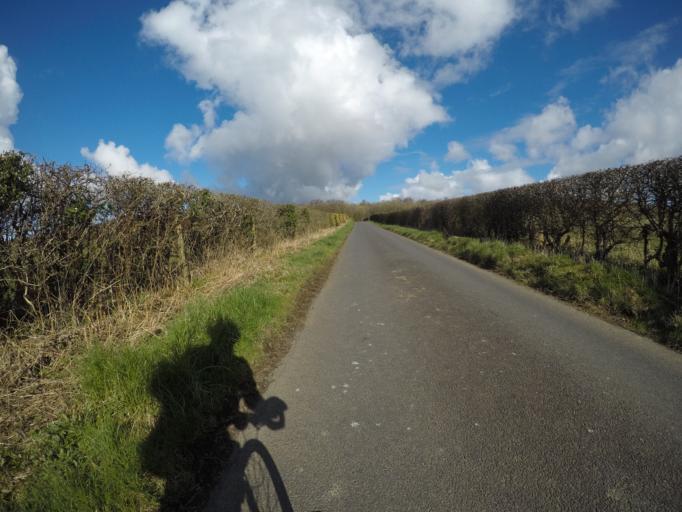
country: GB
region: Scotland
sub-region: North Ayrshire
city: Irvine
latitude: 55.6700
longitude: -4.6525
